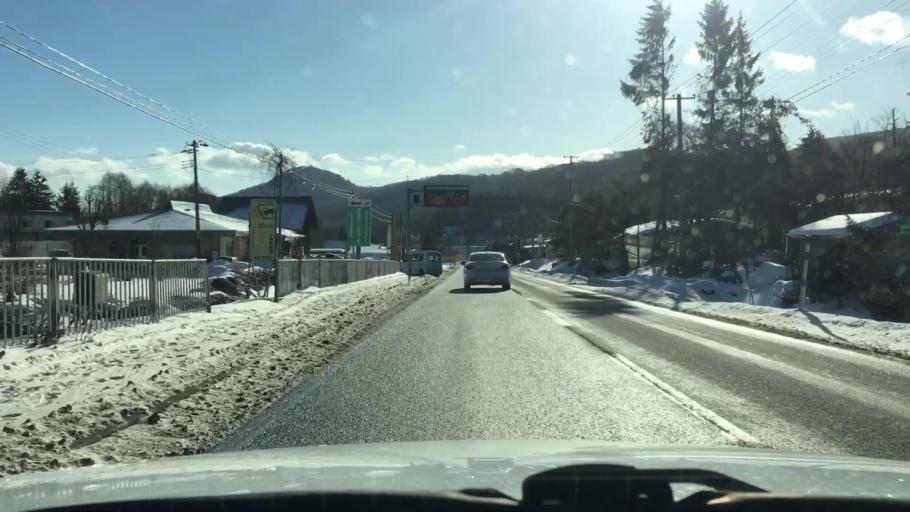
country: JP
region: Iwate
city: Morioka-shi
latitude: 39.6492
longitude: 141.3562
